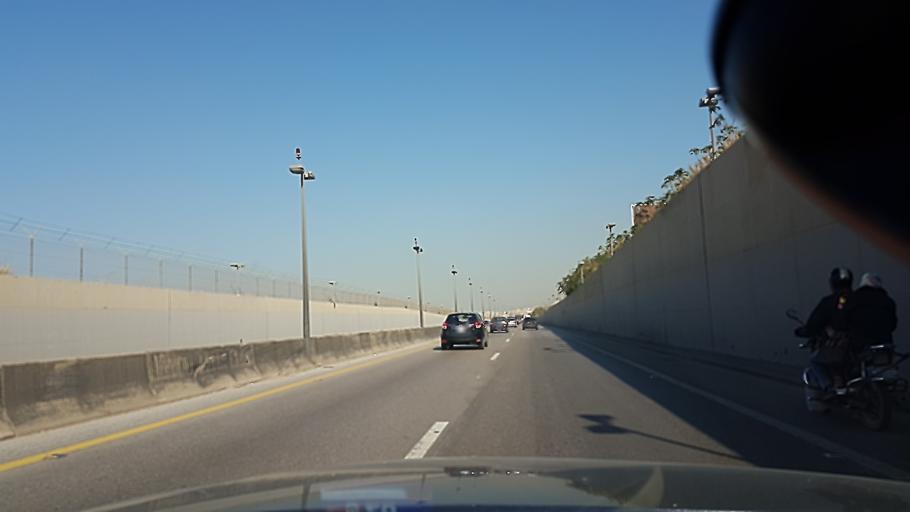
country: LB
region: Mont-Liban
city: Baabda
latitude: 33.8042
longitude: 35.4878
